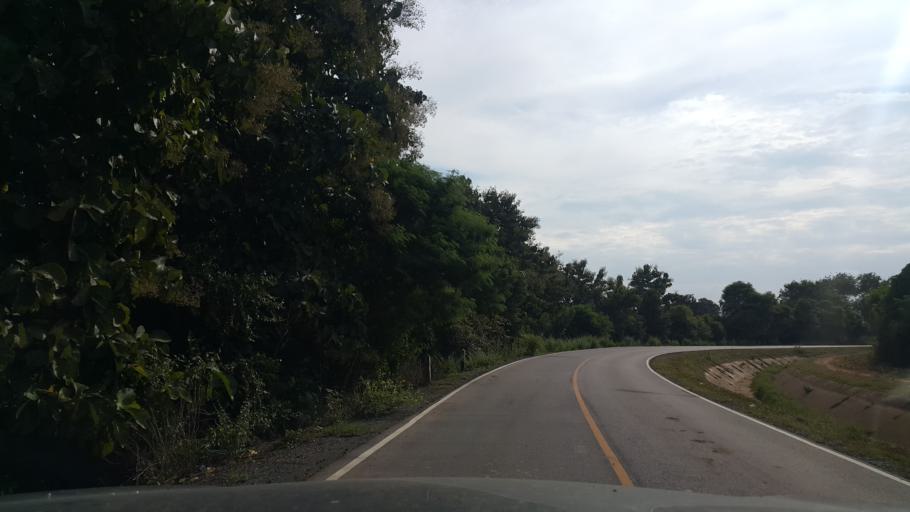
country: TH
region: Chiang Mai
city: San Sai
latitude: 18.9136
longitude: 99.1117
